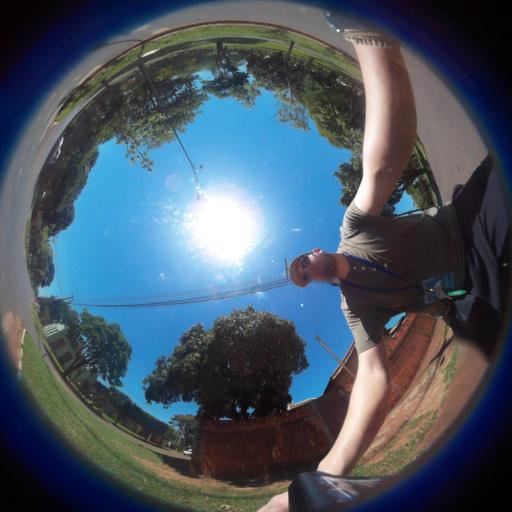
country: BR
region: Mato Grosso do Sul
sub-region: Ponta Pora
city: Ponta Pora
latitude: -22.5260
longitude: -55.7353
